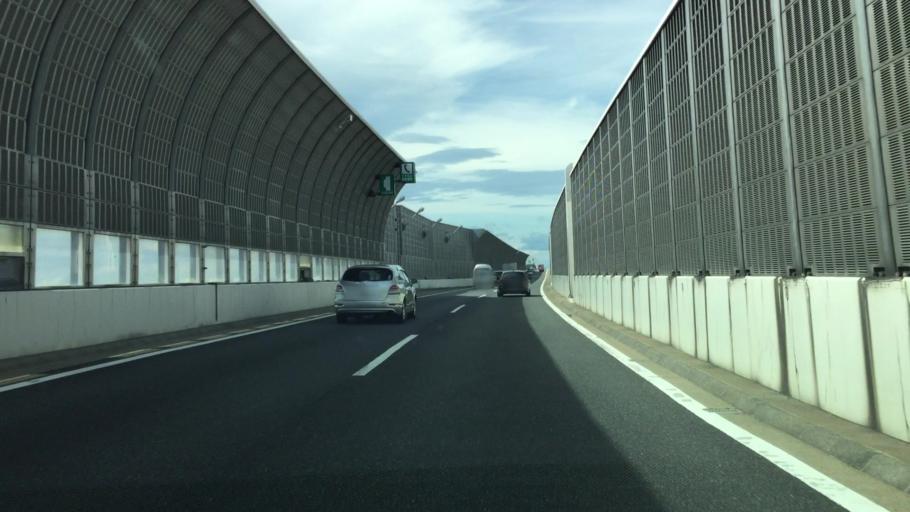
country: JP
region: Saitama
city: Asaka
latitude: 35.8380
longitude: 139.6288
